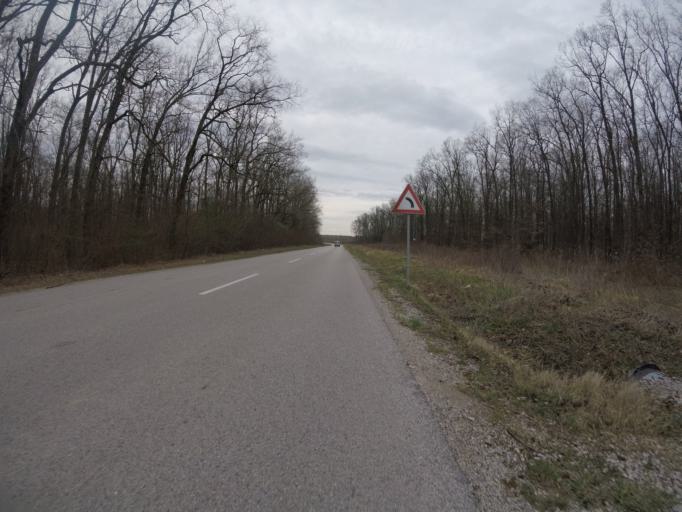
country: HR
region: Zagrebacka
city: Lukavec
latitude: 45.6907
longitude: 15.9817
